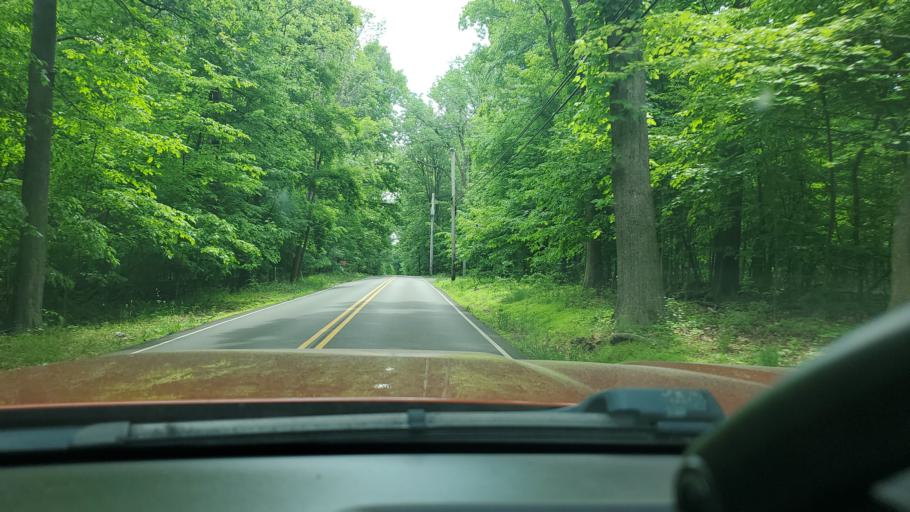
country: US
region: Pennsylvania
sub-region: Montgomery County
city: Red Hill
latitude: 40.3402
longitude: -75.4840
